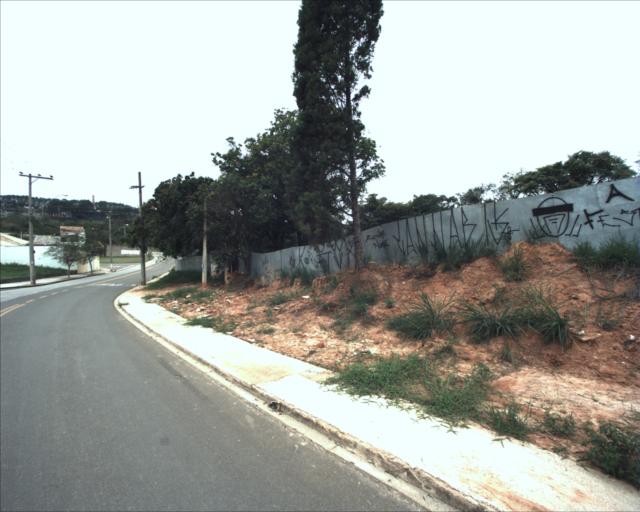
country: BR
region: Sao Paulo
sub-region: Sorocaba
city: Sorocaba
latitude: -23.4536
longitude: -47.3812
